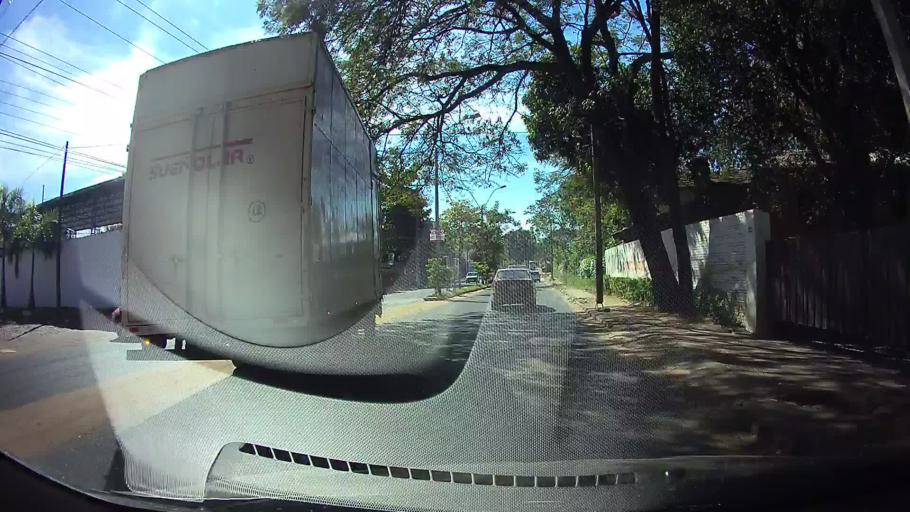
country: PY
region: Central
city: Villa Elisa
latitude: -25.3591
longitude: -57.5732
